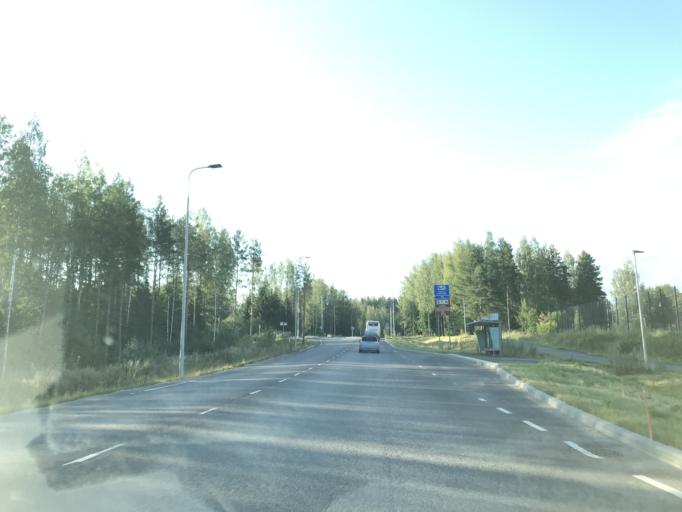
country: FI
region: Uusimaa
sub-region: Helsinki
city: Kauniainen
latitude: 60.3243
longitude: 24.7144
